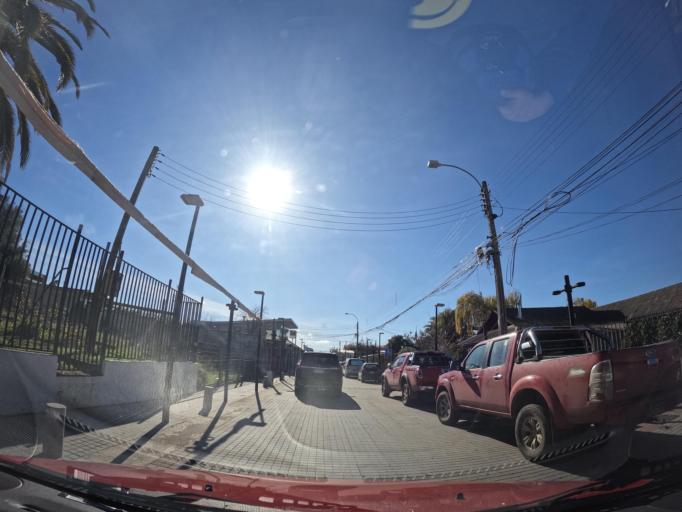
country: CL
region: Maule
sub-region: Provincia de Cauquenes
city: Cauquenes
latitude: -35.9699
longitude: -72.3178
